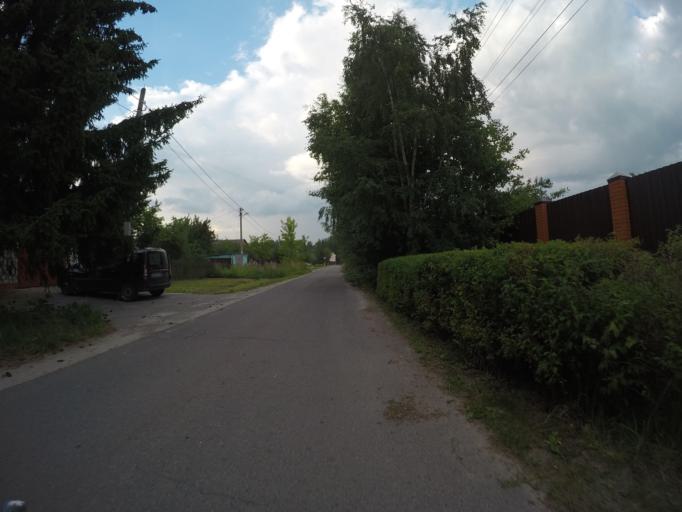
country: RU
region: Moskovskaya
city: Rechitsy
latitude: 55.6011
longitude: 38.5243
